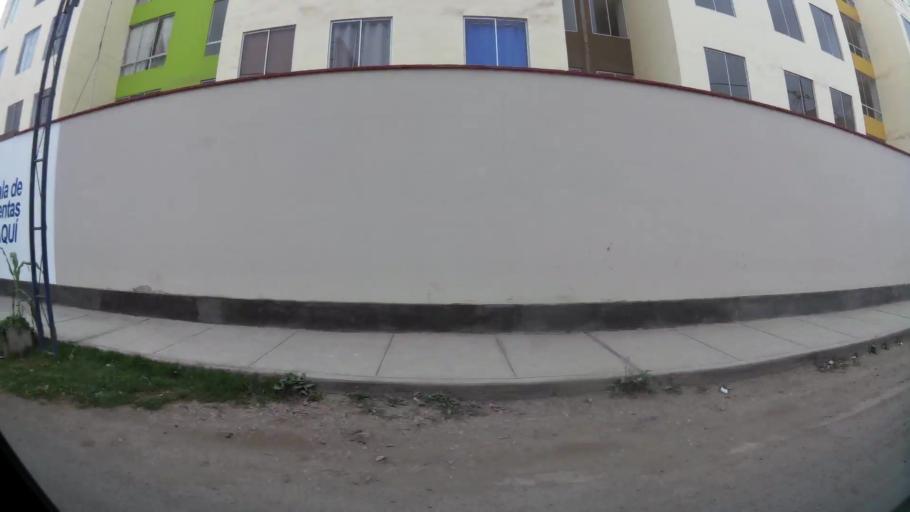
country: PE
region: Lima
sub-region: Lima
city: Independencia
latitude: -11.9526
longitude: -77.0894
